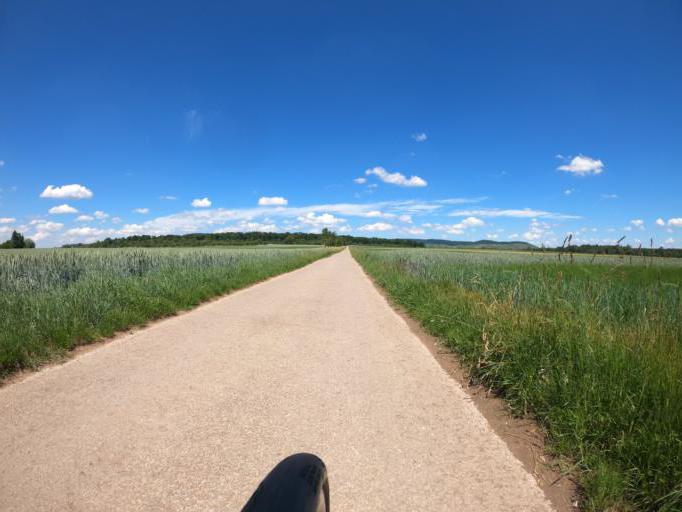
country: DE
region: Baden-Wuerttemberg
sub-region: Regierungsbezirk Stuttgart
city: Sersheim
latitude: 48.9672
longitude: 9.0133
